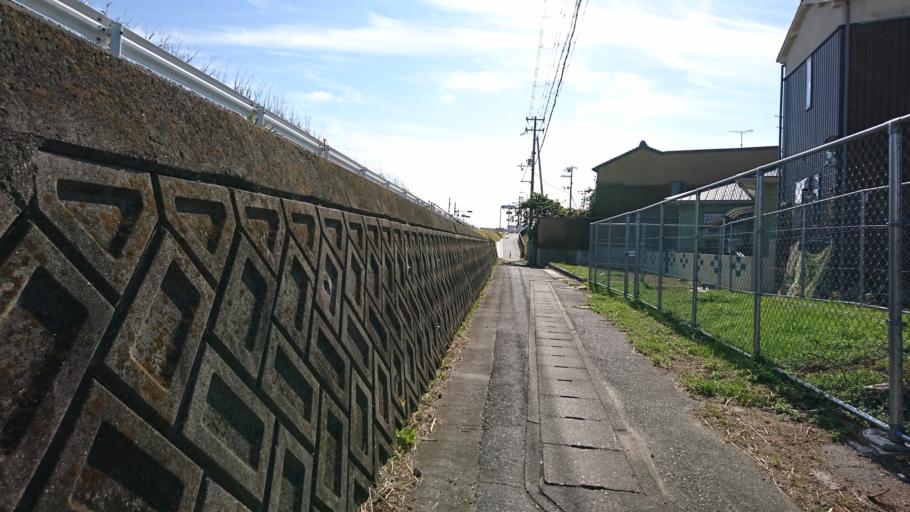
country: JP
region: Hyogo
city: Kakogawacho-honmachi
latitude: 34.7489
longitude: 134.8075
